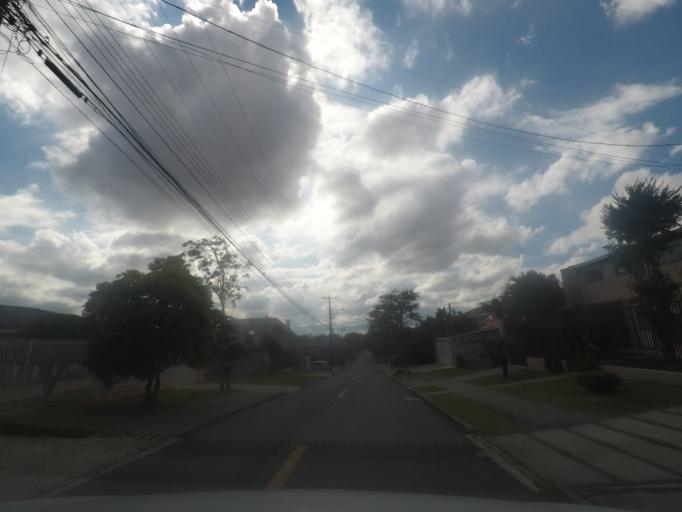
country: BR
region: Parana
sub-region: Pinhais
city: Pinhais
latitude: -25.4647
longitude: -49.2262
